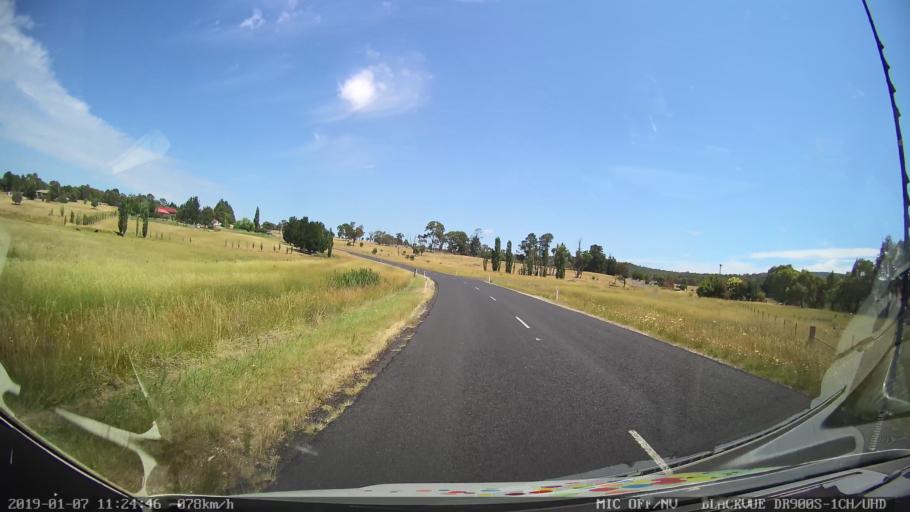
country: AU
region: New South Wales
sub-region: Armidale Dumaresq
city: Armidale
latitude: -30.4631
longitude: 151.6094
